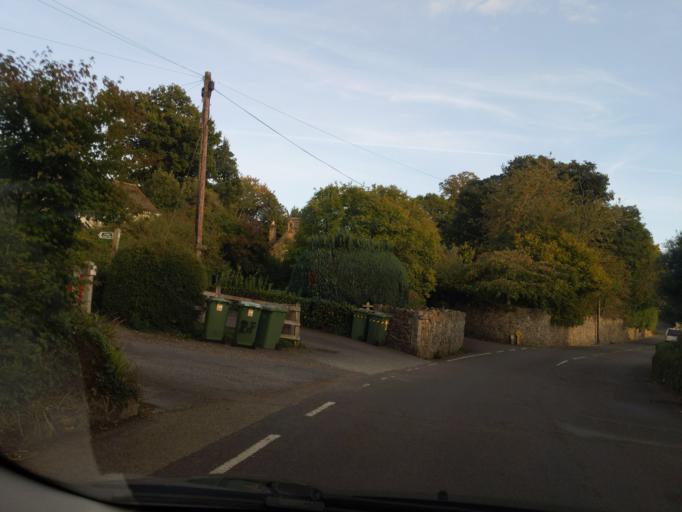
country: GB
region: England
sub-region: Devon
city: Bovey Tracey
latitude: 50.5945
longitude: -3.6667
